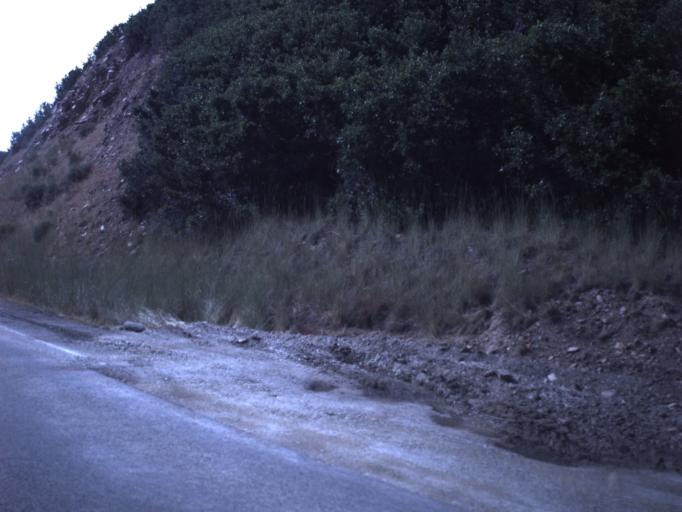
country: US
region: Utah
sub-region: Wasatch County
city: Heber
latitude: 40.4120
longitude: -111.3245
